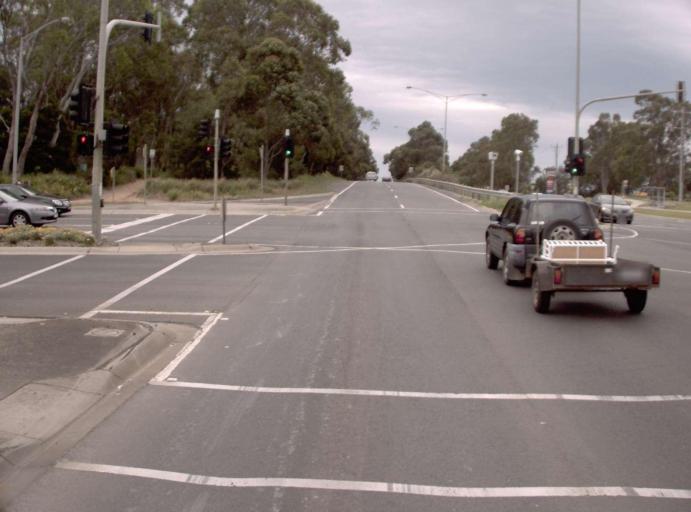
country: AU
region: Victoria
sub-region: Casey
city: Lynbrook
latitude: -38.0502
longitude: 145.2575
